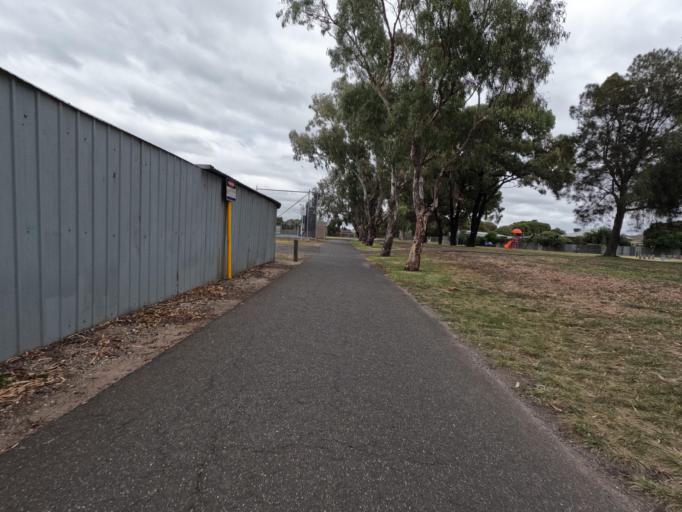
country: AU
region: Victoria
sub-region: Greater Geelong
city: Hamlyn Heights
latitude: -38.1301
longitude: 144.3267
